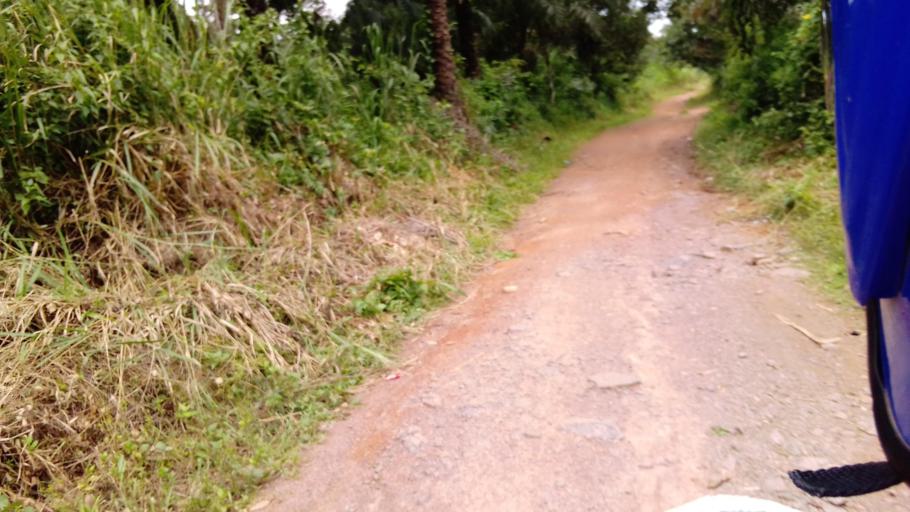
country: SL
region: Eastern Province
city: Koidu
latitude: 8.6594
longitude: -10.9396
